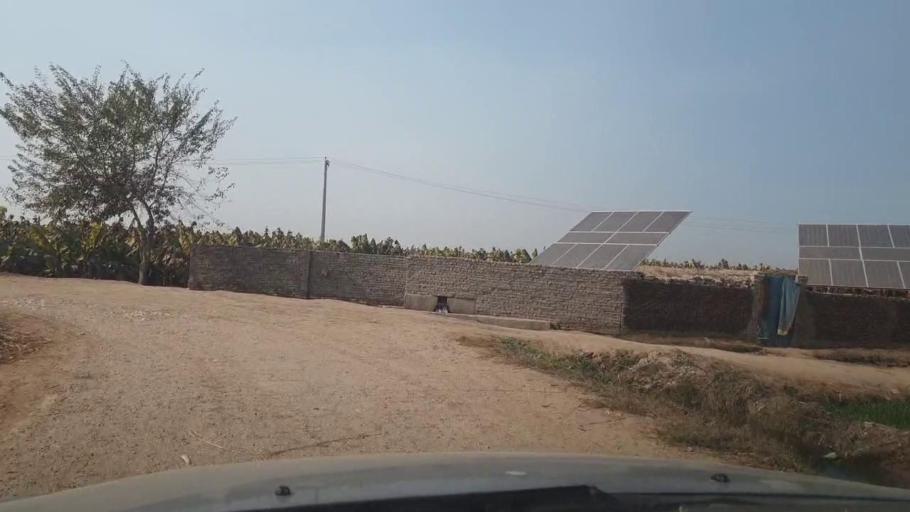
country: PK
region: Sindh
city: Ghotki
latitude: 28.0268
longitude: 69.2582
